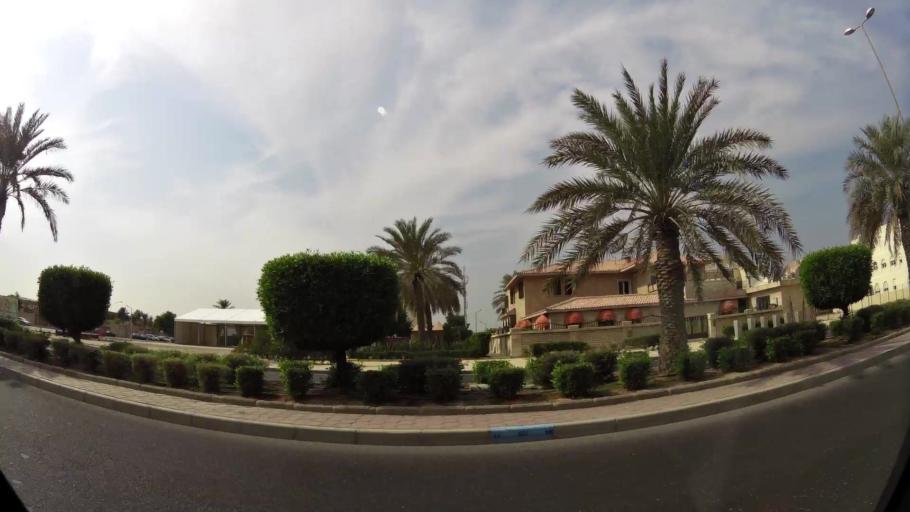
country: KW
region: Al Asimah
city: Ash Shamiyah
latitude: 29.3473
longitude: 47.9795
